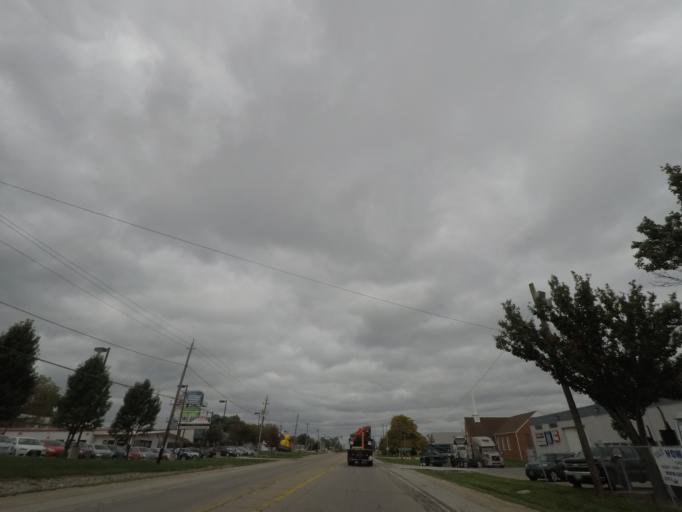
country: US
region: Iowa
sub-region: Polk County
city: Saylorville
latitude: 41.6568
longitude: -93.6005
